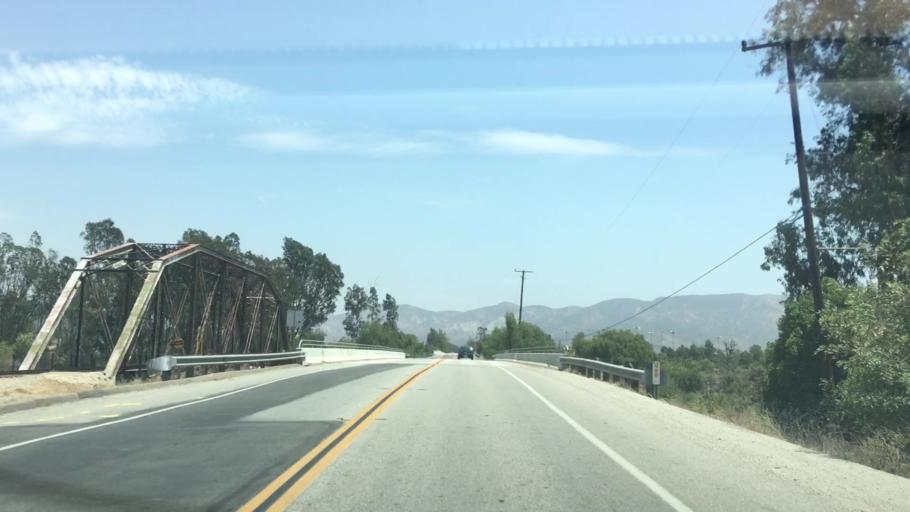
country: US
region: California
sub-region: Ventura County
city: Fillmore
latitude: 34.4075
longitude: -118.9347
